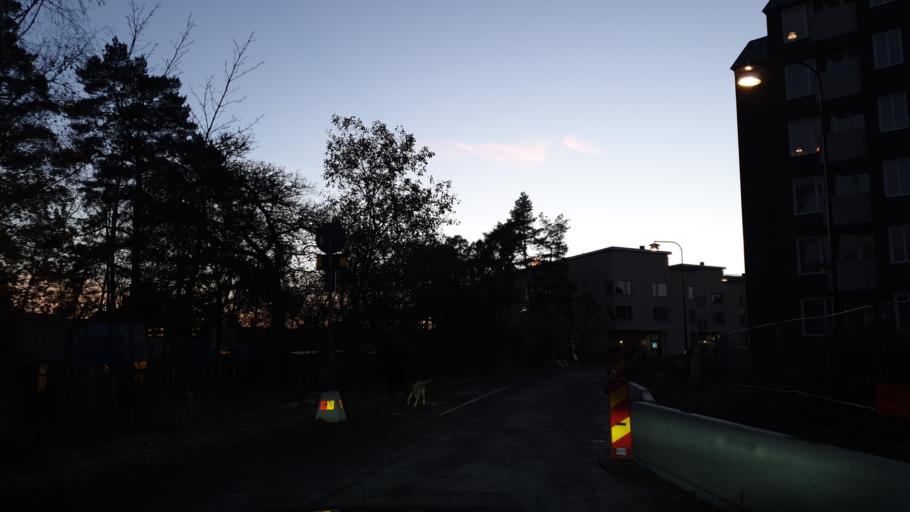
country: SE
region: Stockholm
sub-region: Stockholms Kommun
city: Bromma
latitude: 59.3290
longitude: 17.9187
